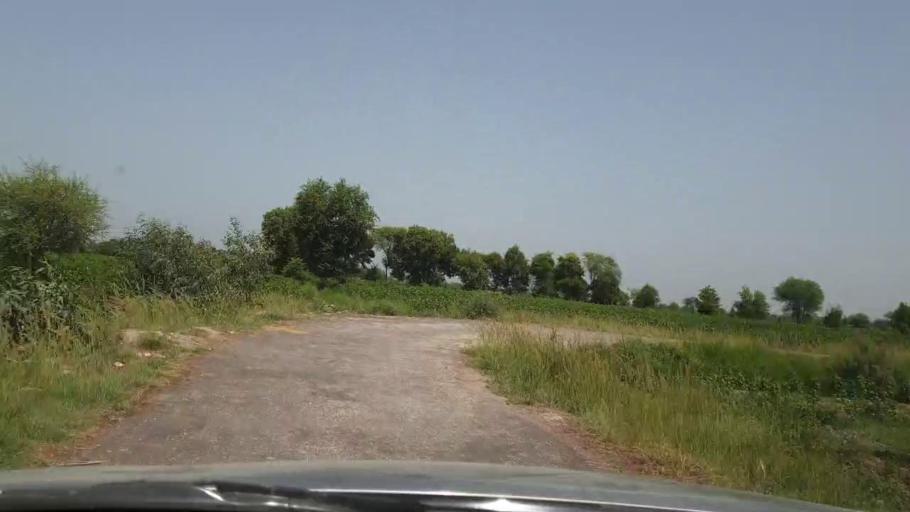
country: PK
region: Sindh
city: Pano Aqil
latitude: 27.8024
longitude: 69.2416
